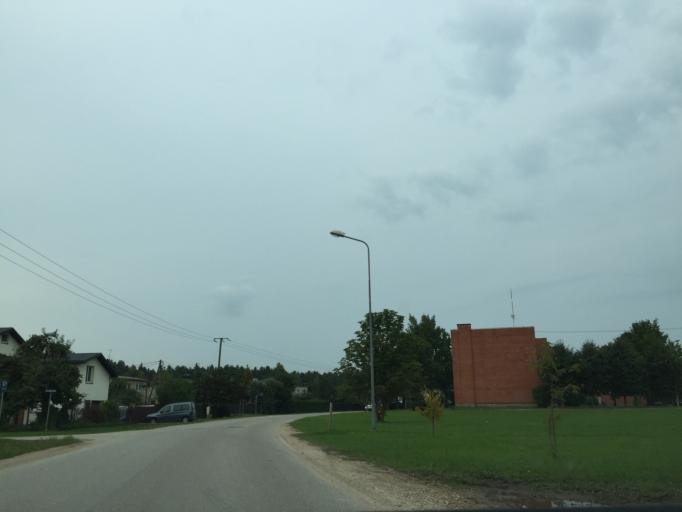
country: LV
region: Ogre
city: Ogre
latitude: 56.8141
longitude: 24.6439
